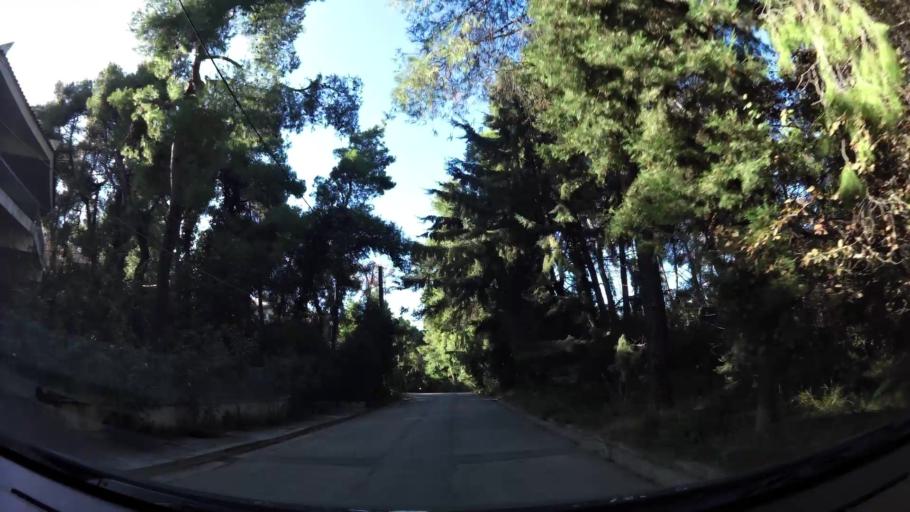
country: GR
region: Attica
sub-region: Nomarchia Anatolikis Attikis
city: Drosia
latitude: 38.1156
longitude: 23.8566
